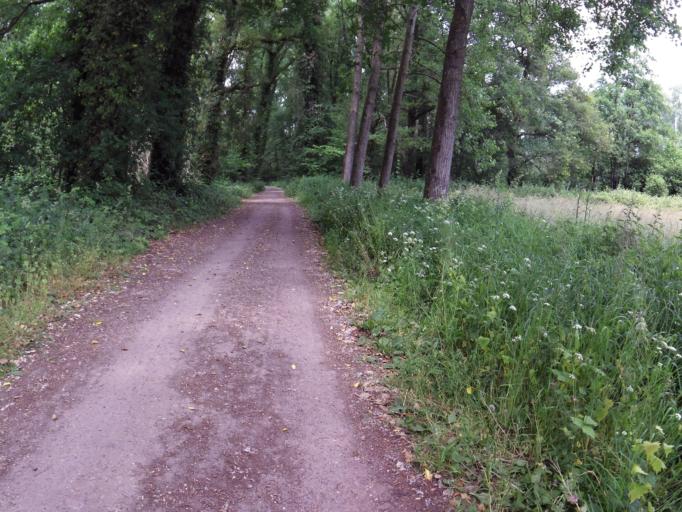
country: NL
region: North Brabant
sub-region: Gemeente Oirschot
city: Oirschot
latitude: 51.5368
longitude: 5.3430
